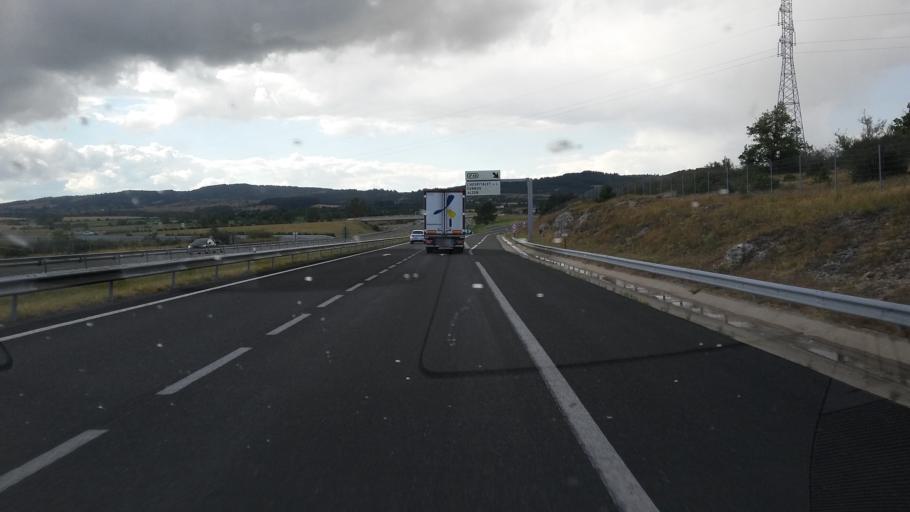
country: FR
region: Midi-Pyrenees
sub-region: Departement de l'Aveyron
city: La Cavalerie
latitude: 43.9478
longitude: 3.2193
